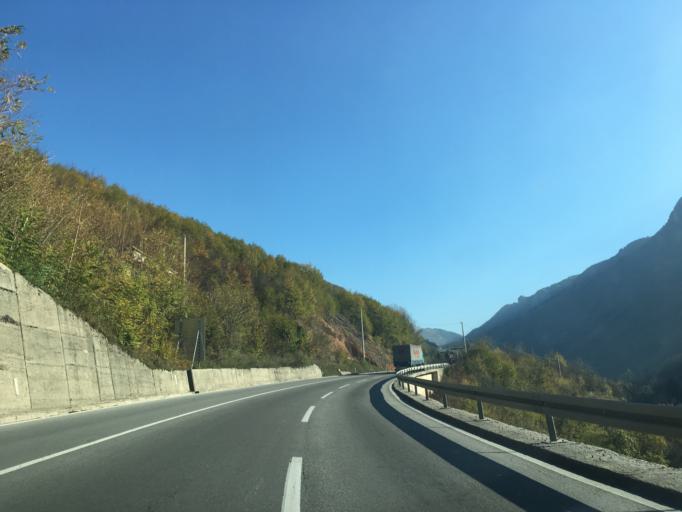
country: BA
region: Federation of Bosnia and Herzegovina
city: Kobilja Glava
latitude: 43.8561
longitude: 18.4570
